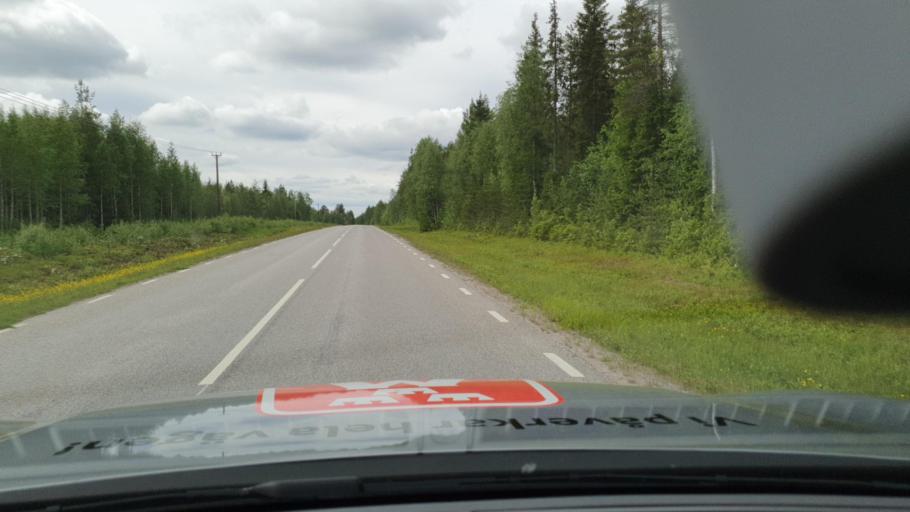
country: FI
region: Lapland
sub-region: Torniolaakso
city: Ylitornio
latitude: 66.0350
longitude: 23.5215
